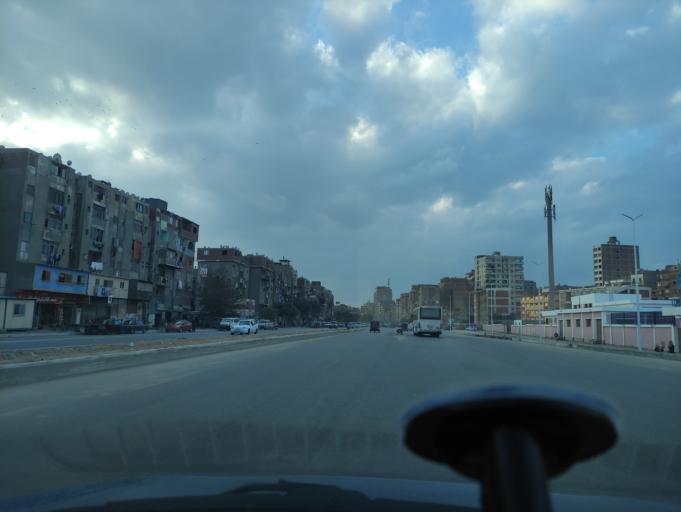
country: EG
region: Muhafazat al Qalyubiyah
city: Al Khankah
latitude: 30.1356
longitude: 31.3535
